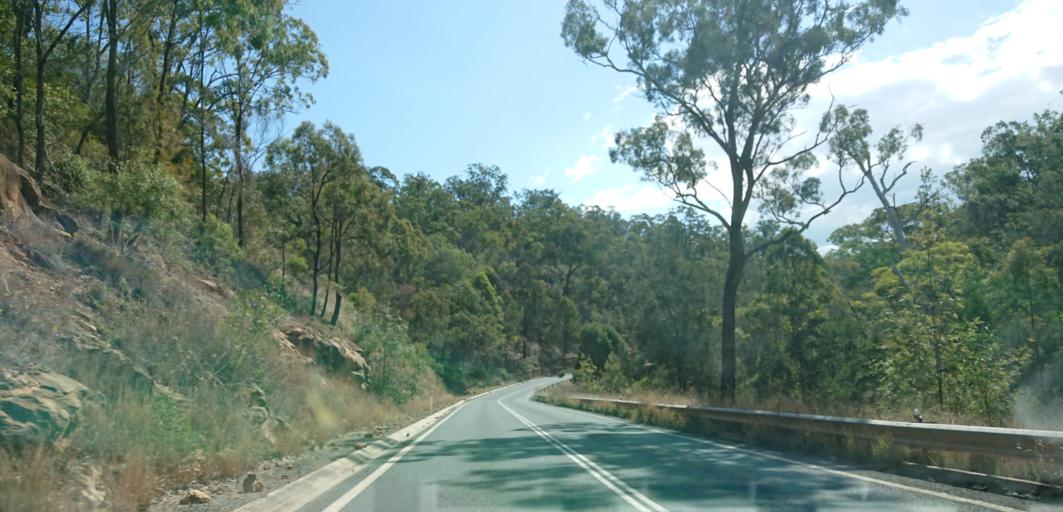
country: AU
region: Queensland
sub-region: Toowoomba
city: Top Camp
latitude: -27.7784
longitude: 152.0966
